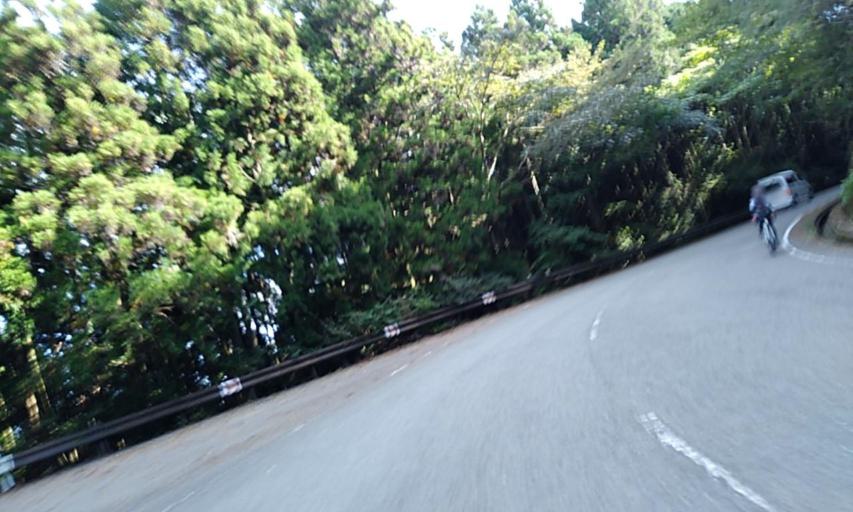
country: JP
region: Wakayama
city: Iwade
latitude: 34.1163
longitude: 135.3428
